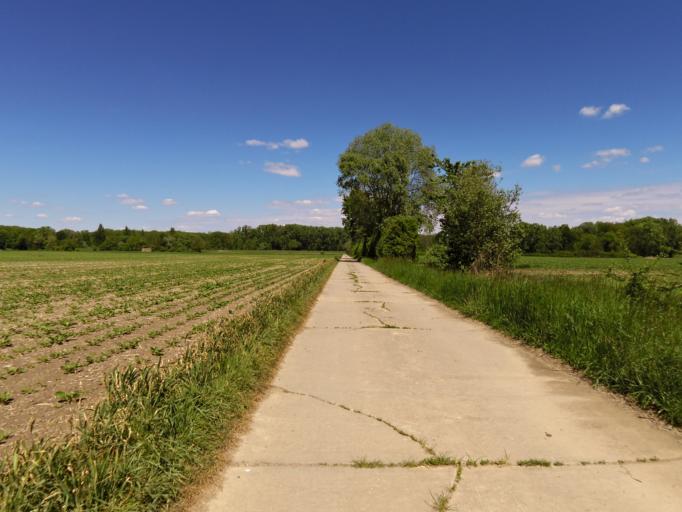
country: DE
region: Rheinland-Pfalz
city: Eich
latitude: 49.6945
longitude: 8.3838
